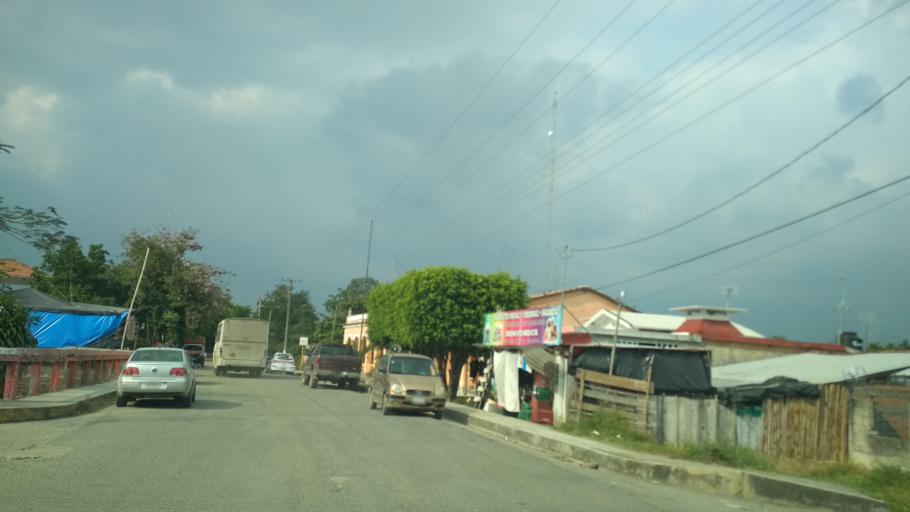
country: MM
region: Kayah
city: Loikaw
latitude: 20.2378
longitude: 97.2767
